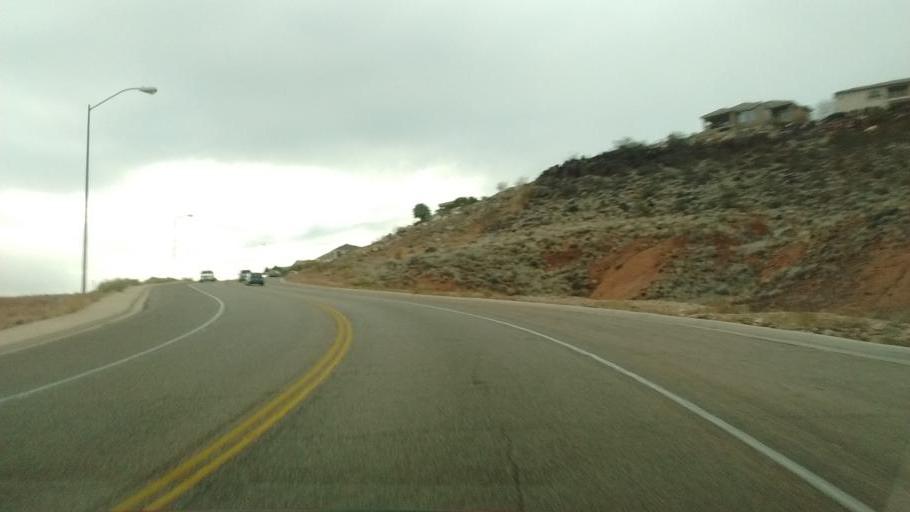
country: US
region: Utah
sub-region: Washington County
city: Saint George
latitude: 37.0971
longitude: -113.5429
